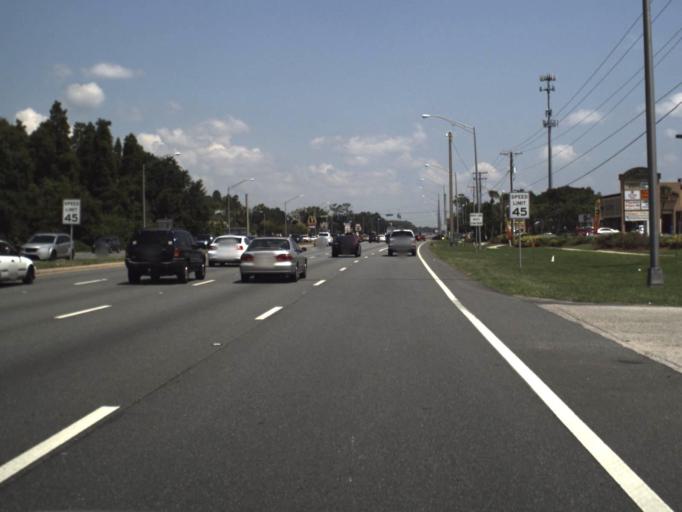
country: US
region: Florida
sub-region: Hillsborough County
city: Carrollwood
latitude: 28.0412
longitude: -82.5047
